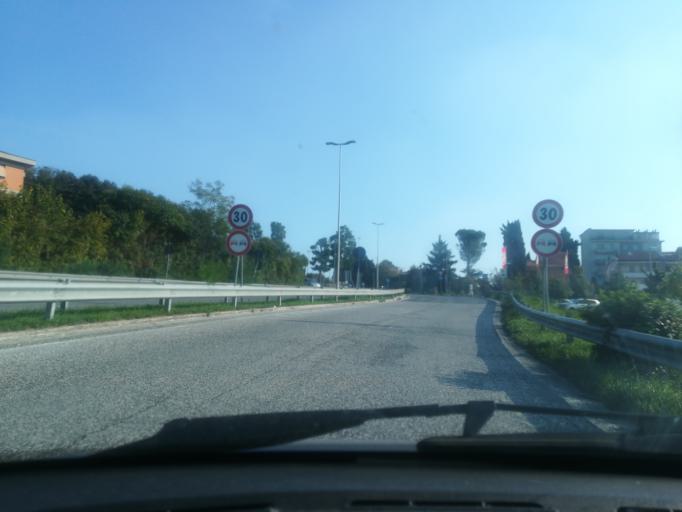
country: IT
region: The Marches
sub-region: Provincia di Macerata
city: Macerata
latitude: 43.2913
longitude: 13.4555
